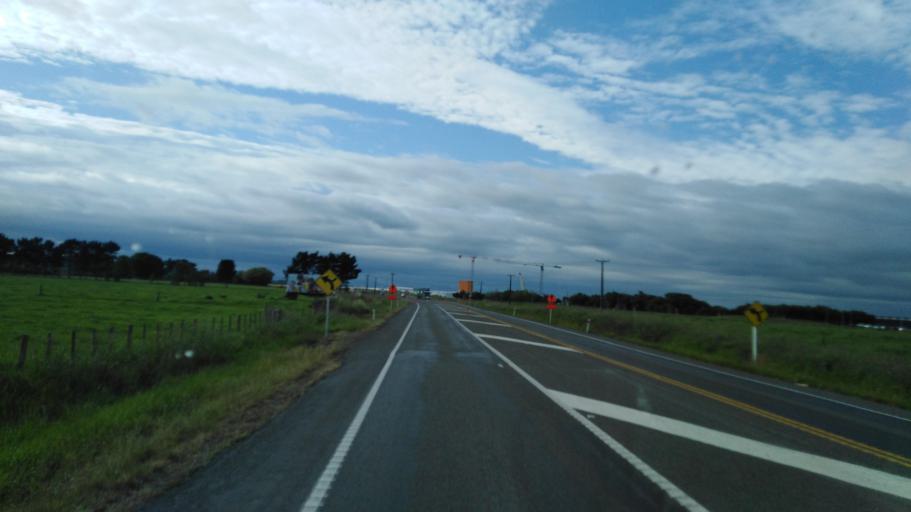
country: NZ
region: Manawatu-Wanganui
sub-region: Rangitikei District
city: Bulls
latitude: -40.1967
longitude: 175.3912
